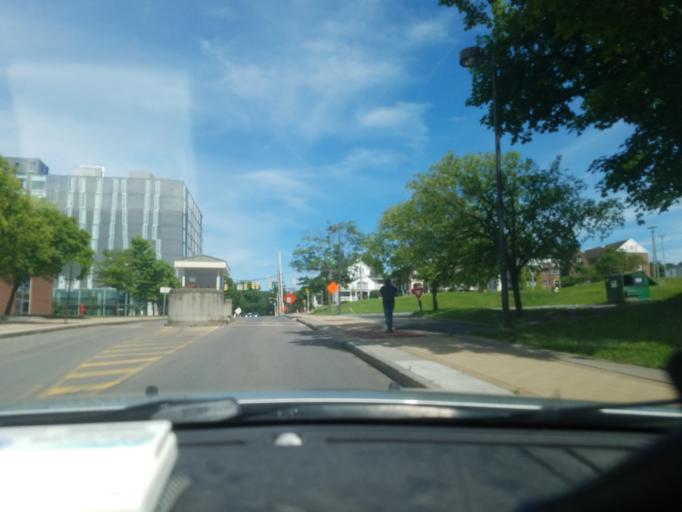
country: US
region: New York
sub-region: Onondaga County
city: Syracuse
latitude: 43.0394
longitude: -76.1312
